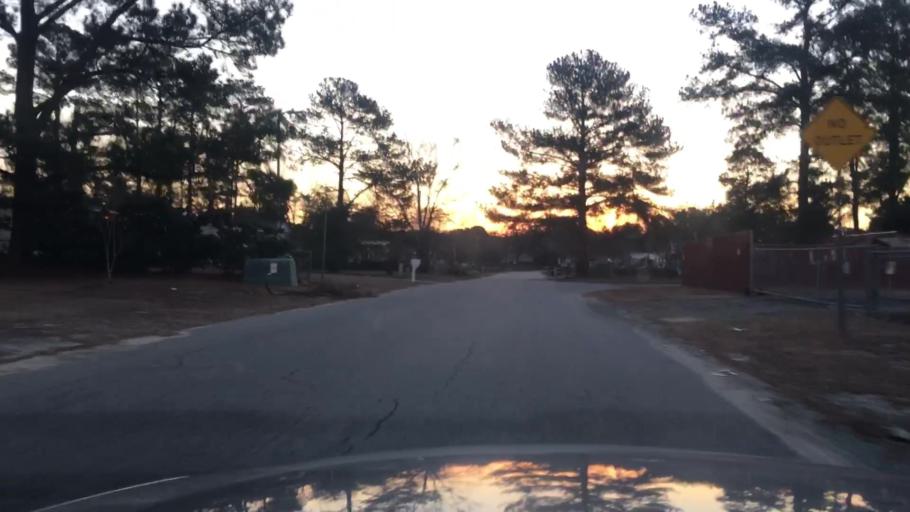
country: US
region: North Carolina
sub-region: Cumberland County
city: Hope Mills
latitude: 34.9909
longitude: -78.9024
